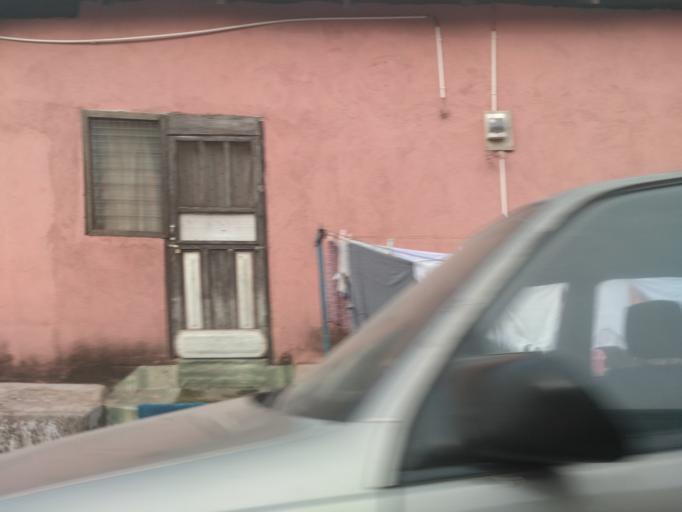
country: GH
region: Ashanti
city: Kumasi
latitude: 6.6793
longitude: -1.5921
